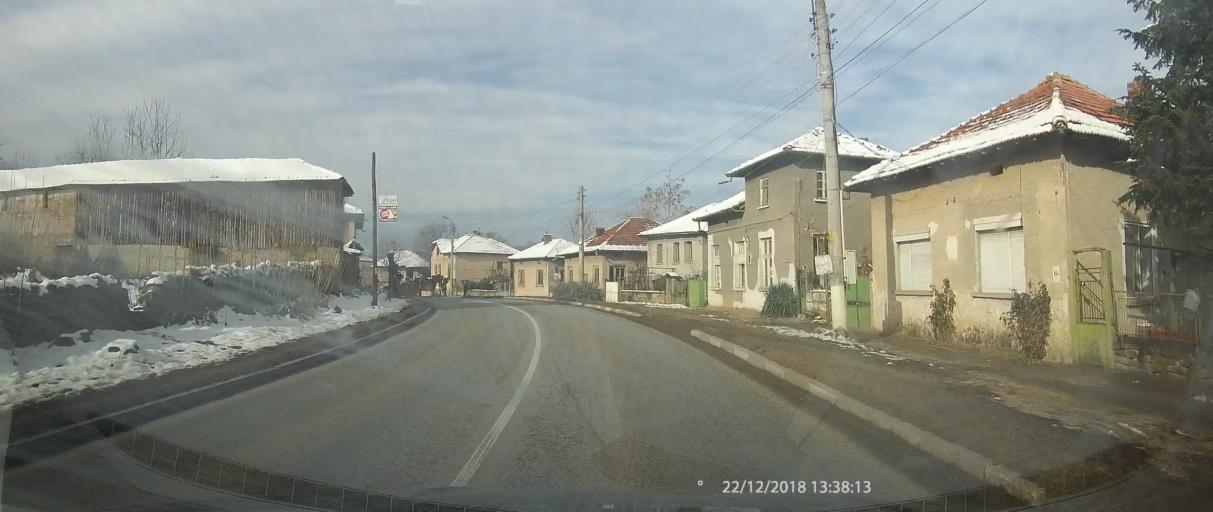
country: BG
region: Lovech
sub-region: Obshtina Lukovit
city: Lukovit
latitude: 43.1532
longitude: 24.1529
